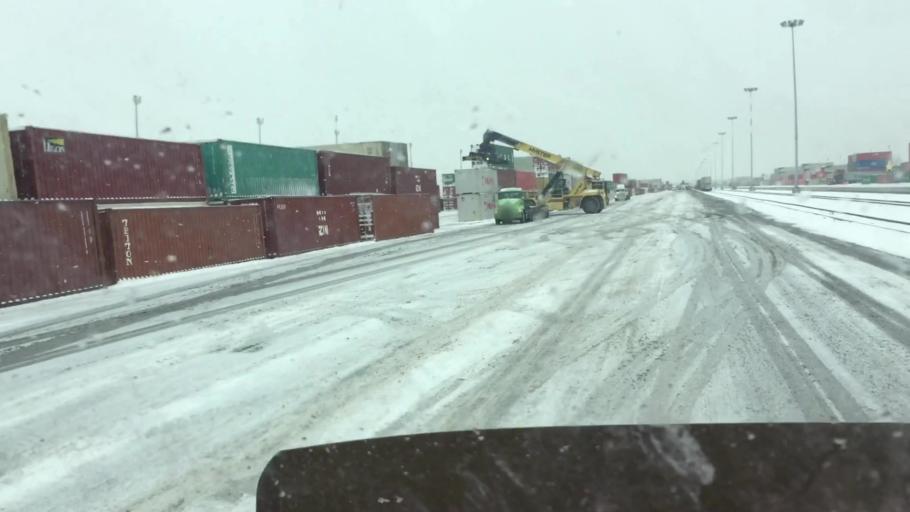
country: CA
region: Quebec
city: Cote-Saint-Luc
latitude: 45.4603
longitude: -73.6927
